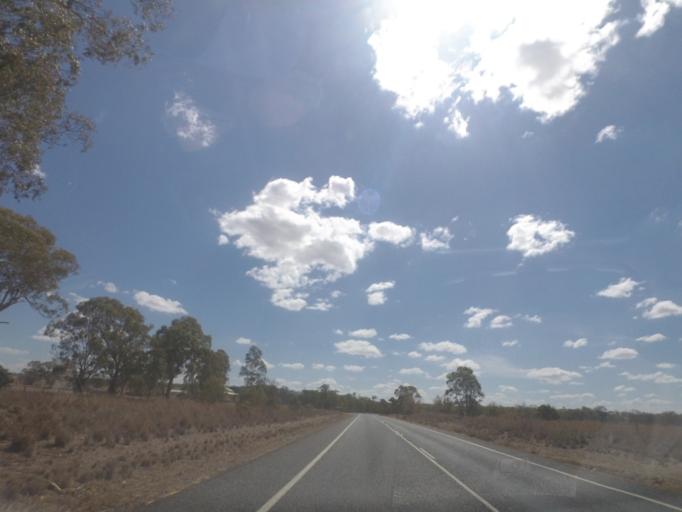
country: AU
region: Queensland
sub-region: Southern Downs
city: Warwick
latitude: -28.1624
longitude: 151.7028
